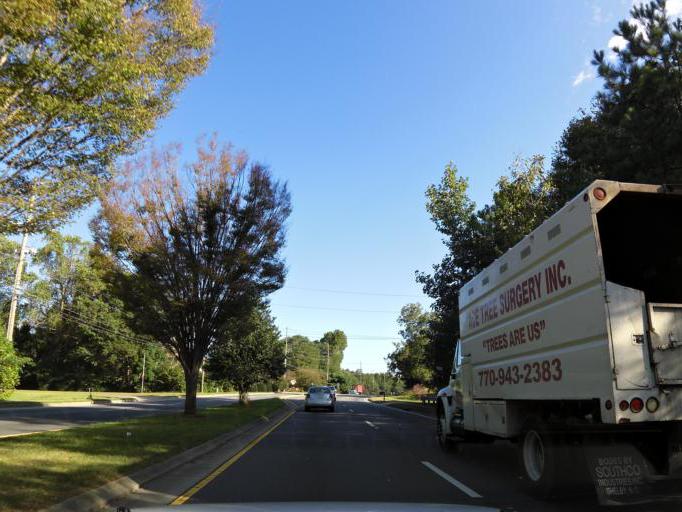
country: US
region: Georgia
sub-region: Cobb County
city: Kennesaw
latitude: 33.9527
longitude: -84.6230
